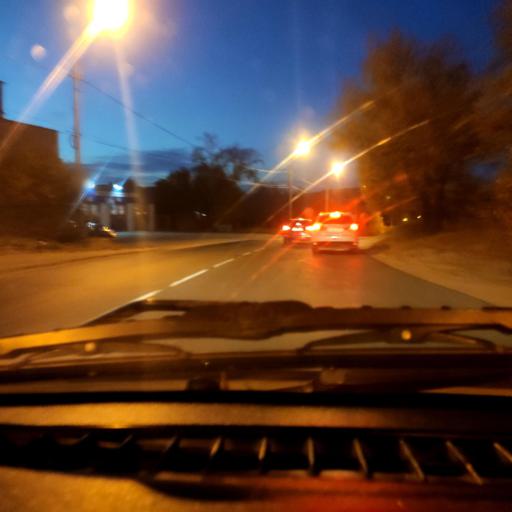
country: RU
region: Samara
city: Zhigulevsk
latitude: 53.4670
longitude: 49.5486
